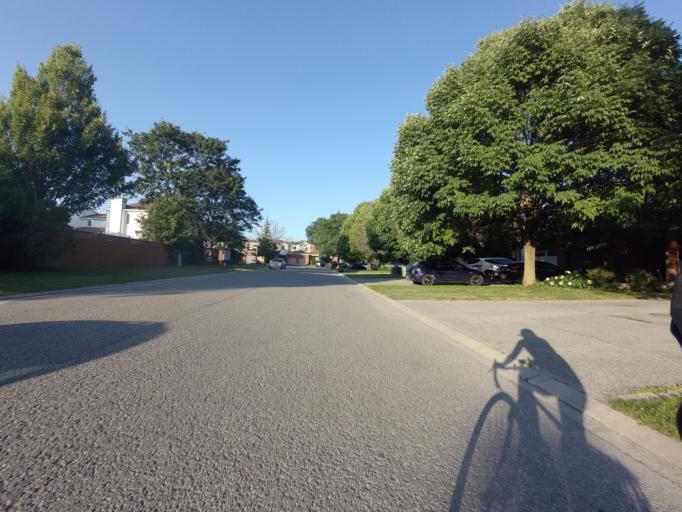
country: CA
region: Ontario
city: Bells Corners
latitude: 45.2879
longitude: -75.7371
